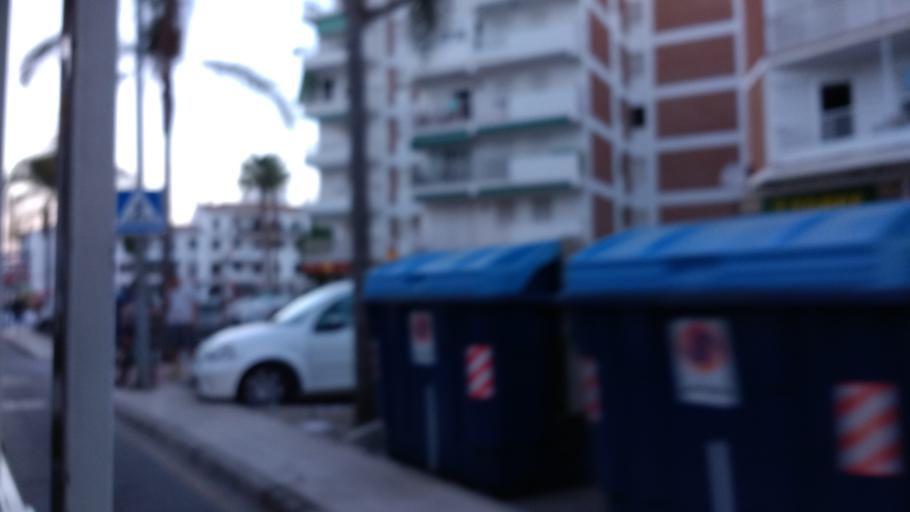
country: ES
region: Andalusia
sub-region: Provincia de Malaga
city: Velez-Malaga
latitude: 36.7436
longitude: -4.0888
